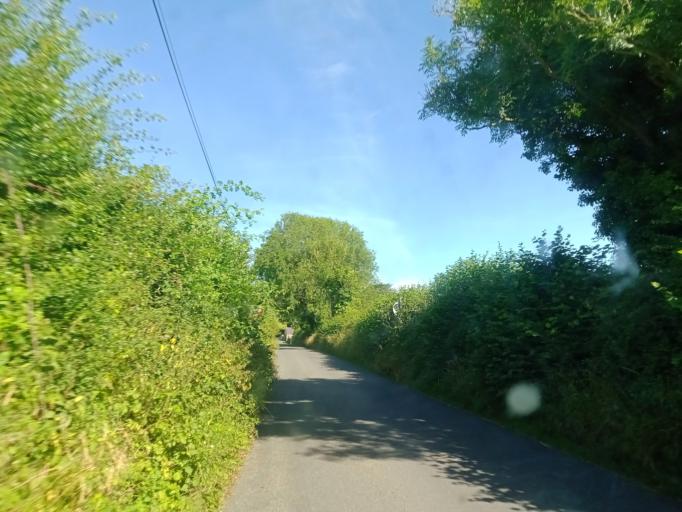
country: IE
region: Leinster
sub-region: Kilkenny
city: Ballyragget
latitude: 52.7558
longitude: -7.4026
